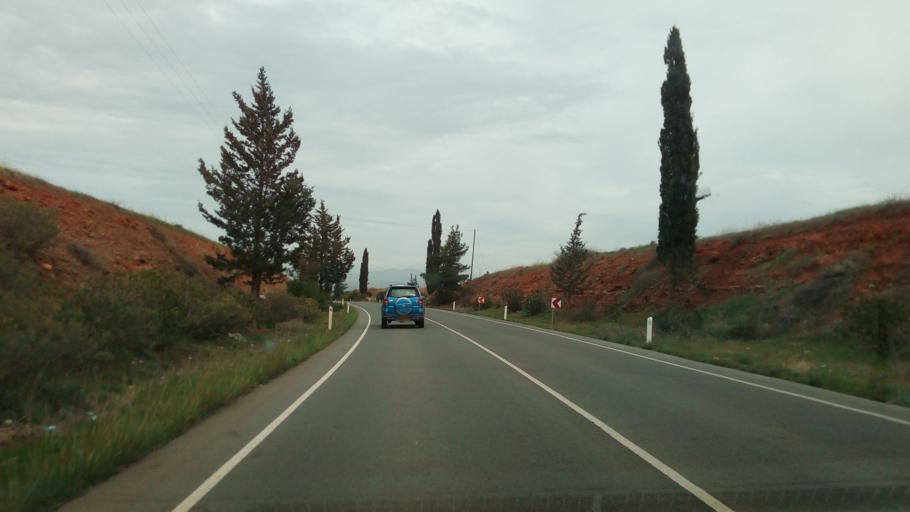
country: CY
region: Lefkosia
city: Astromeritis
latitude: 35.1180
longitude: 33.0077
